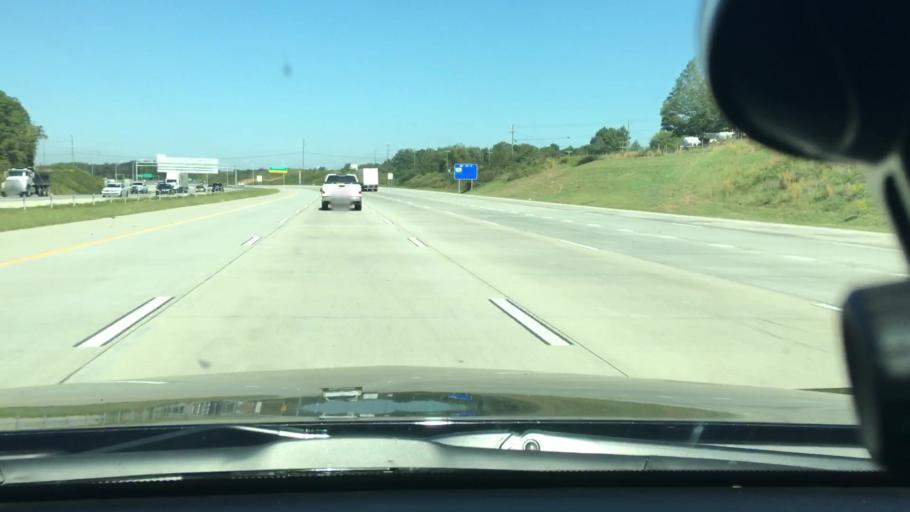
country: US
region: North Carolina
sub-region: Cabarrus County
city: Harrisburg
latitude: 35.3565
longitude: -80.7401
